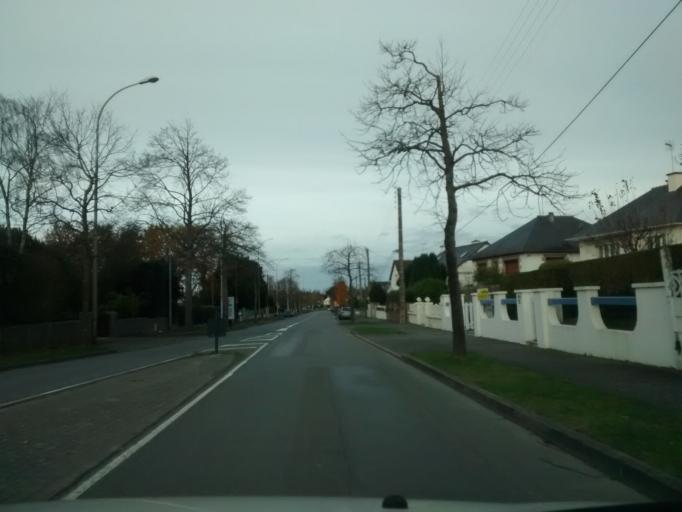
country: FR
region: Brittany
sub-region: Departement d'Ille-et-Vilaine
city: Dinard
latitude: 48.6254
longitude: -2.0692
